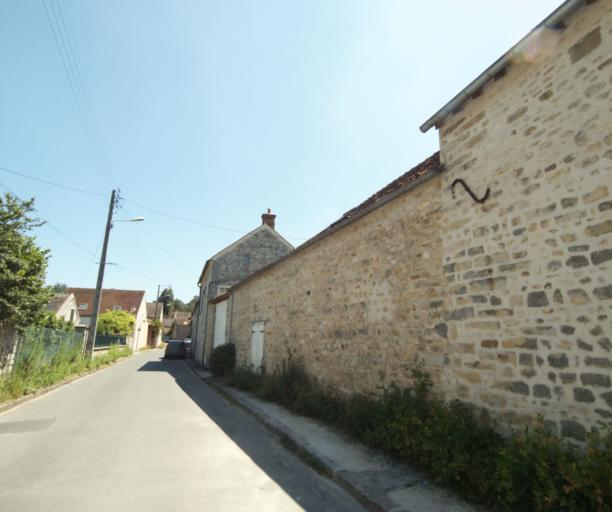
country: FR
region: Ile-de-France
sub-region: Departement de Seine-et-Marne
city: Noisy-sur-Ecole
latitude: 48.3751
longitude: 2.4805
